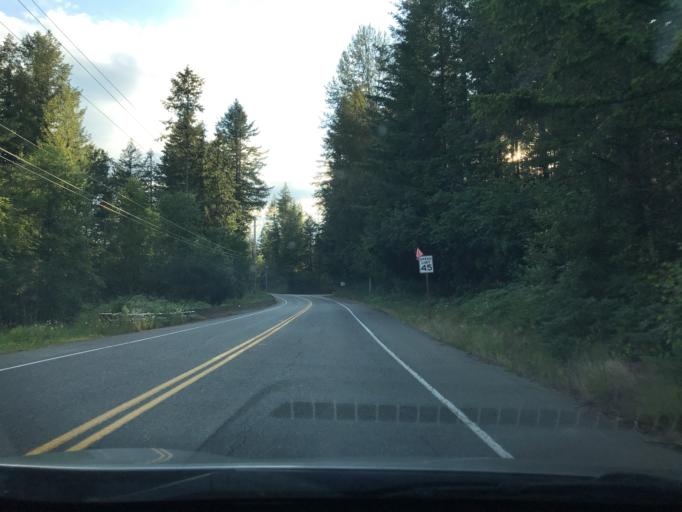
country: US
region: Washington
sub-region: King County
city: Black Diamond
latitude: 47.3109
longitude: -122.0378
